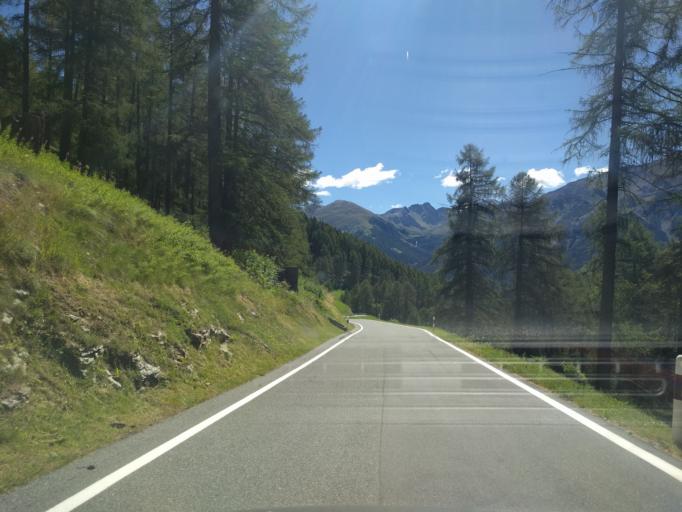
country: IT
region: Trentino-Alto Adige
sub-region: Bolzano
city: Tubre
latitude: 46.6184
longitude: 10.3720
